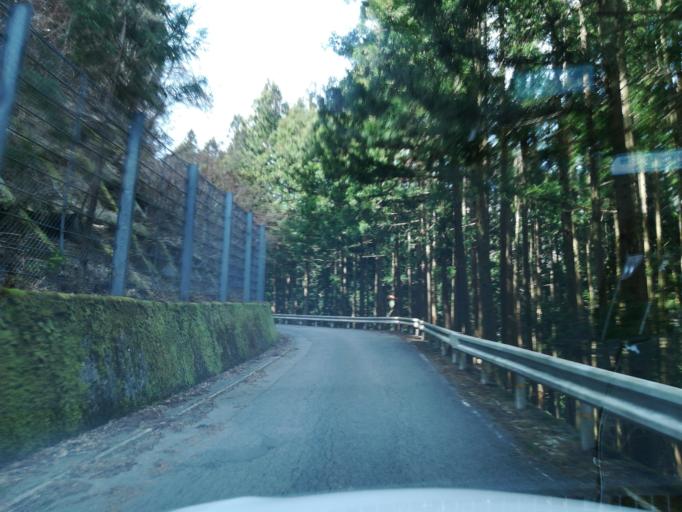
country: JP
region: Tokushima
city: Wakimachi
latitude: 33.8889
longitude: 134.0617
